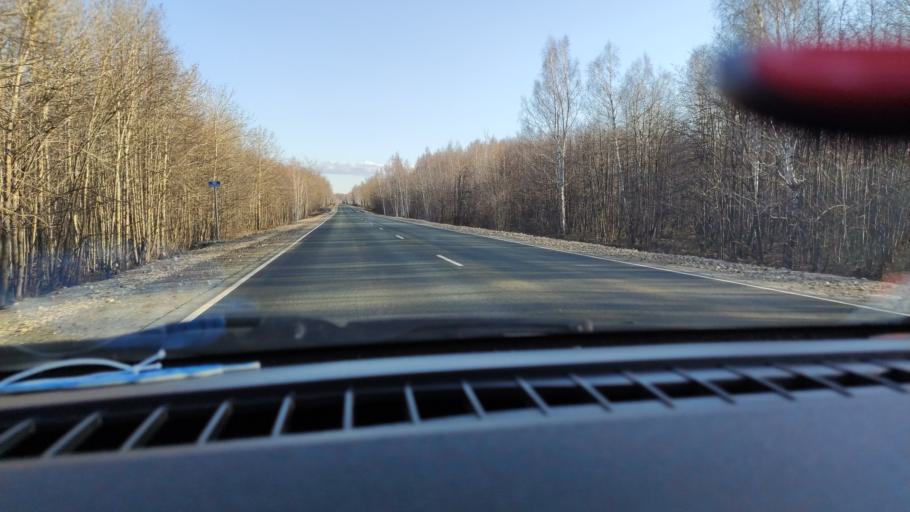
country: RU
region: Saratov
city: Khvalynsk
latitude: 52.4312
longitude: 48.0089
